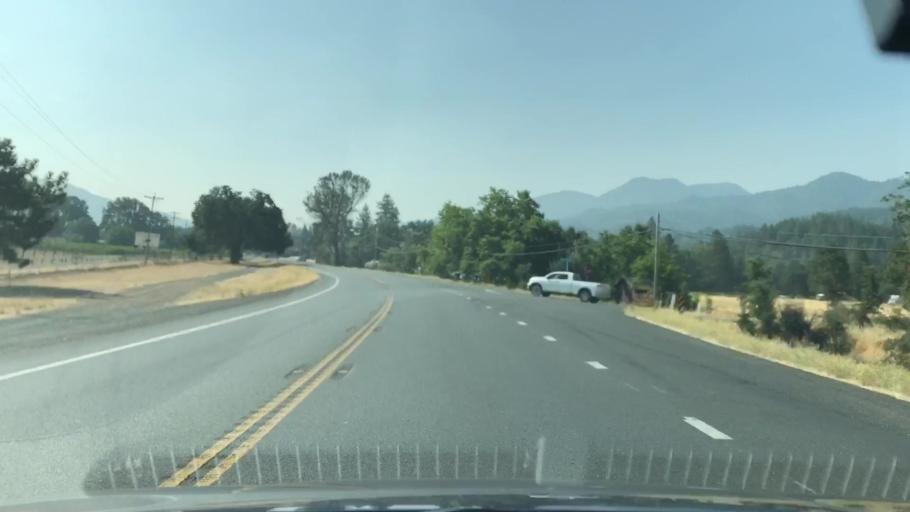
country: US
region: California
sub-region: Lake County
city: Middletown
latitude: 38.7370
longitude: -122.6263
